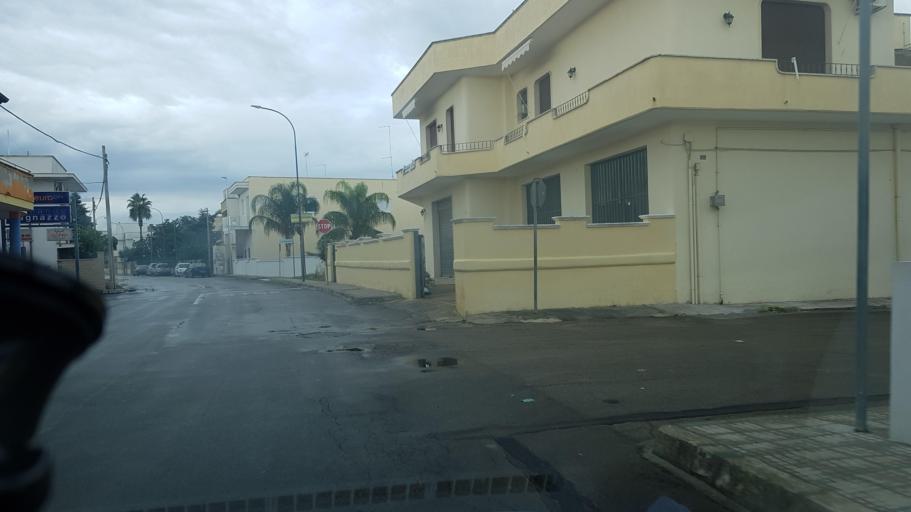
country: IT
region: Apulia
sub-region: Provincia di Lecce
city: Salice Salentino
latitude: 40.3901
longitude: 17.9594
